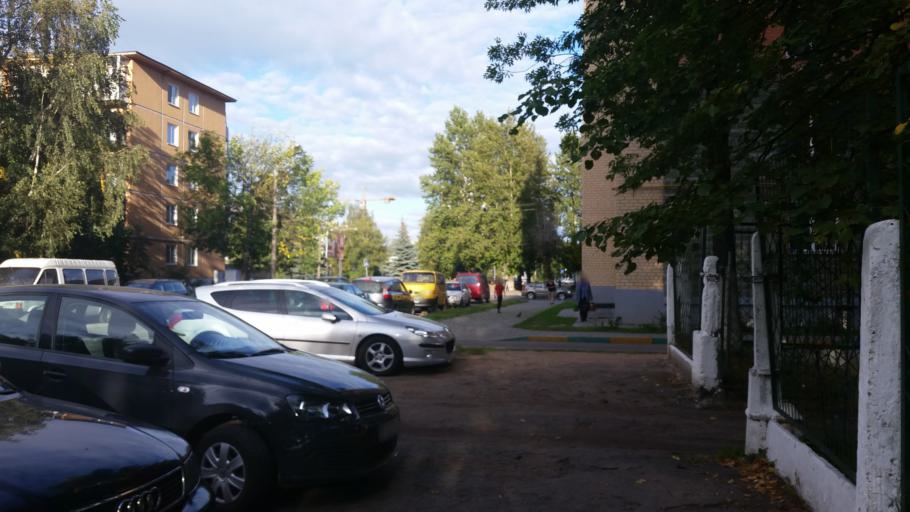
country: BY
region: Vitebsk
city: Vitebsk
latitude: 55.1830
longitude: 30.1878
